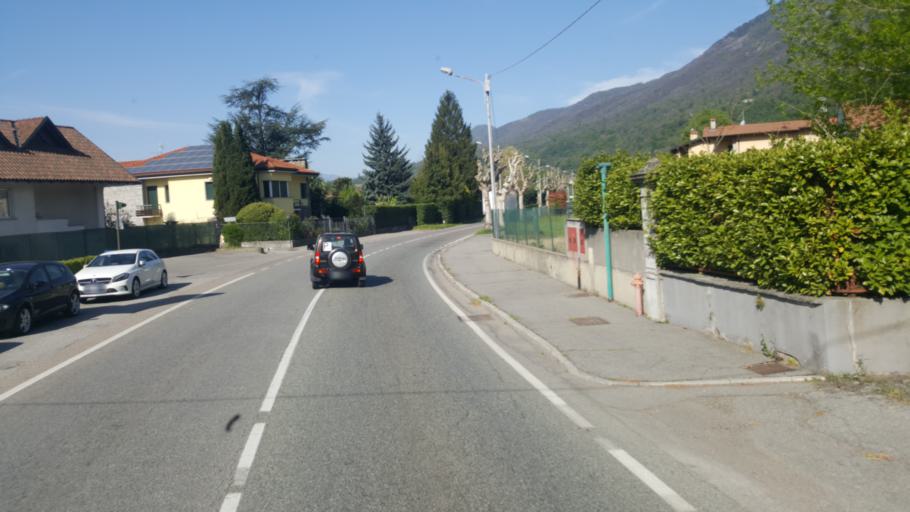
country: IT
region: Lombardy
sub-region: Provincia di Varese
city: Cuveglio
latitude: 45.9043
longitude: 8.7319
